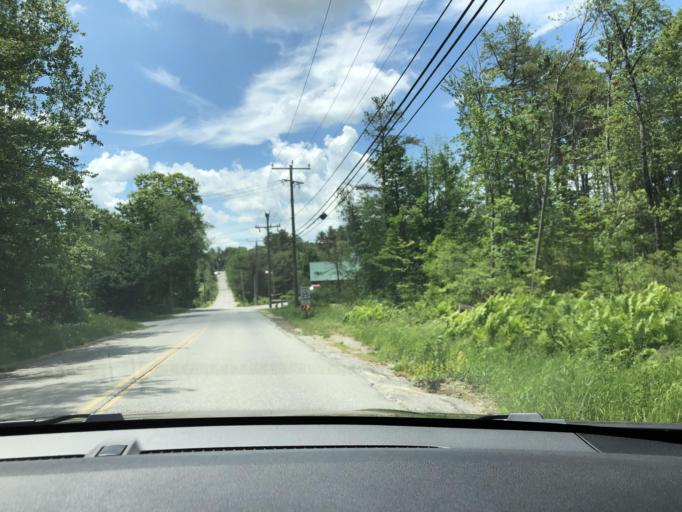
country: US
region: New Hampshire
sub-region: Merrimack County
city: New London
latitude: 43.4108
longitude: -71.9879
